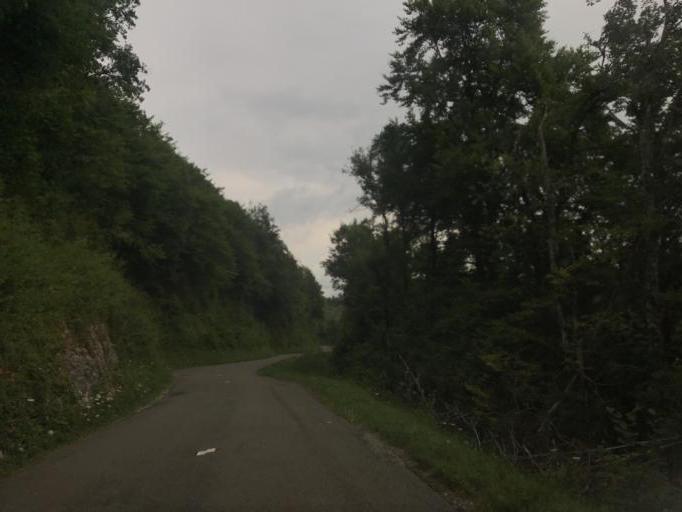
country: FR
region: Franche-Comte
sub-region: Departement du Jura
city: Lavans-les-Saint-Claude
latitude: 46.3305
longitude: 5.7622
